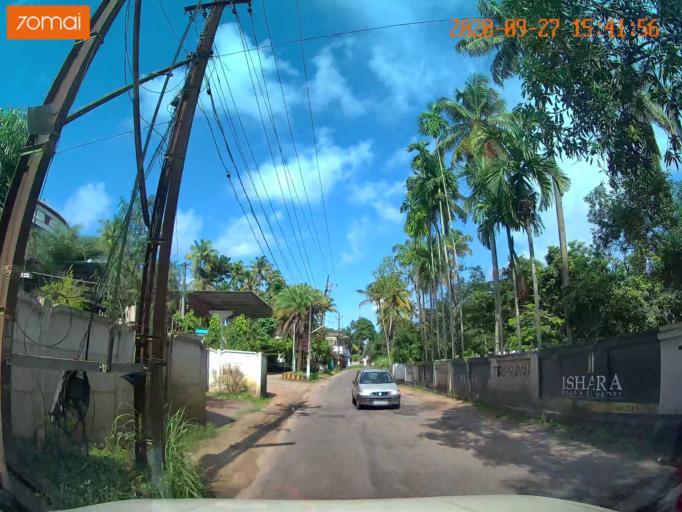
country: IN
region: Kerala
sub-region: Thrissur District
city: Thanniyam
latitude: 10.4723
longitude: 76.0991
